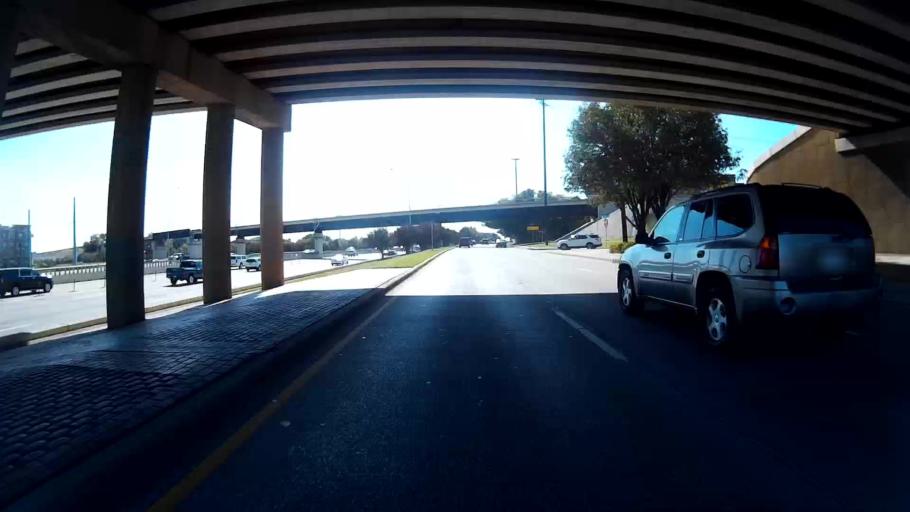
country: US
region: Texas
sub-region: Dallas County
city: Richardson
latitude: 32.9679
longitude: -96.7213
